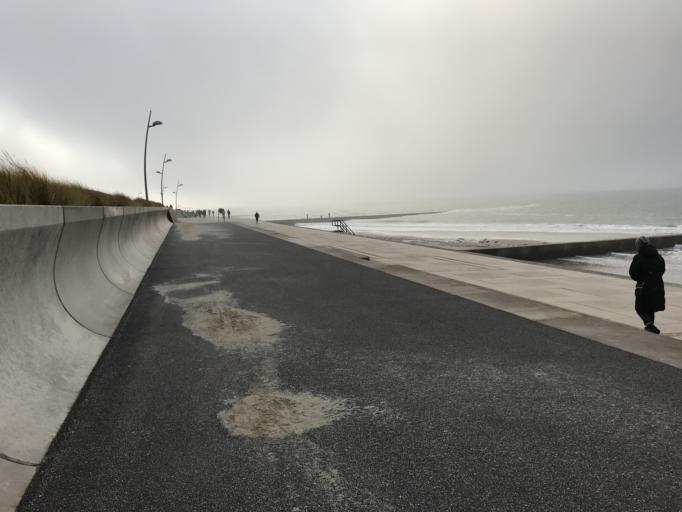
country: DE
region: Lower Saxony
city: Borkum
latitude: 53.5868
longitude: 6.6572
